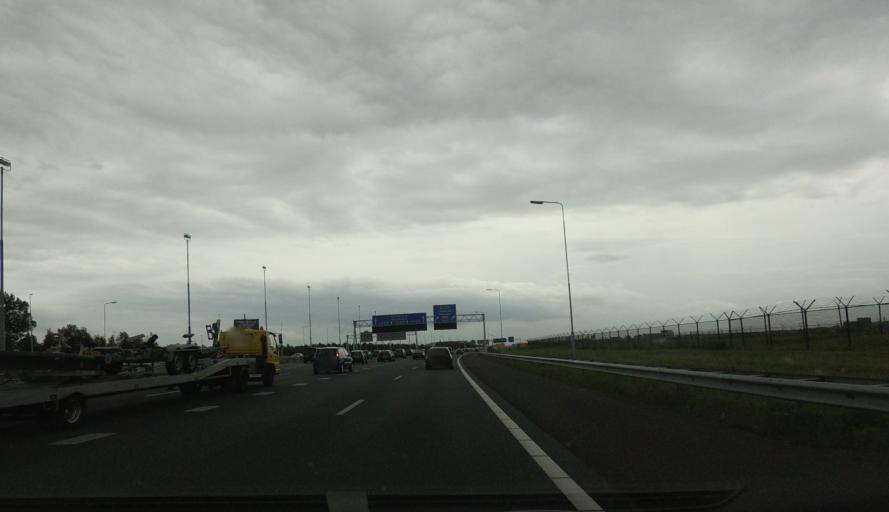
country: NL
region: North Holland
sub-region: Gemeente Aalsmeer
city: Aalsmeer
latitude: 52.2999
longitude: 4.7423
